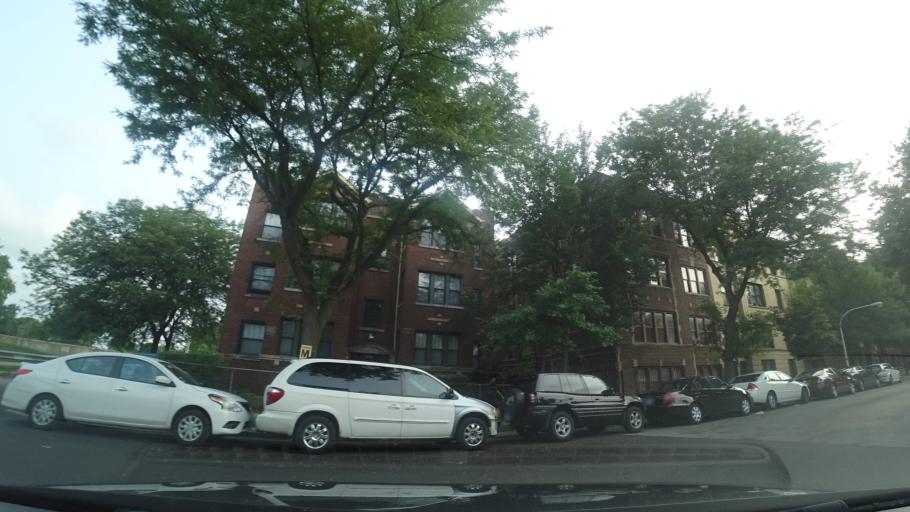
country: US
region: Illinois
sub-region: Cook County
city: Evanston
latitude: 42.0225
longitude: -87.6742
